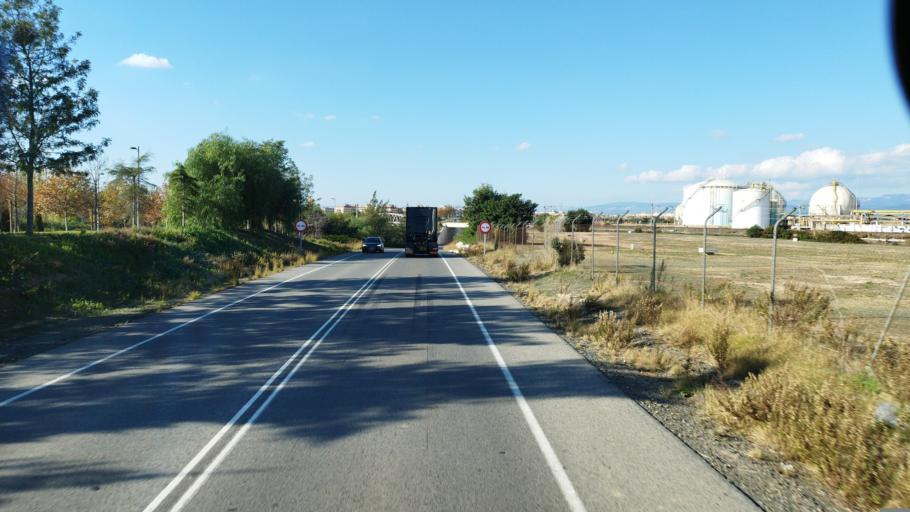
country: ES
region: Catalonia
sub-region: Provincia de Tarragona
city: Vila-seca
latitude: 41.1018
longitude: 1.1627
